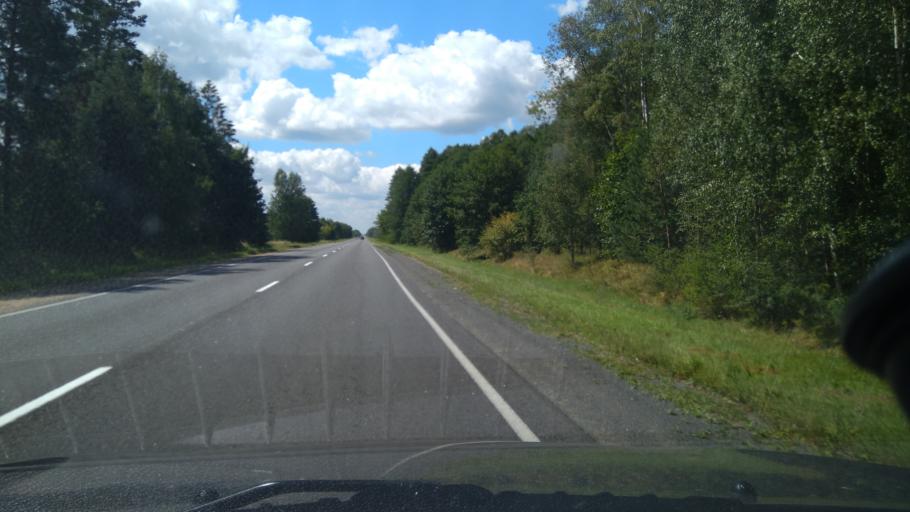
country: BY
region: Brest
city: Nyakhachava
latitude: 52.6568
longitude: 25.2315
